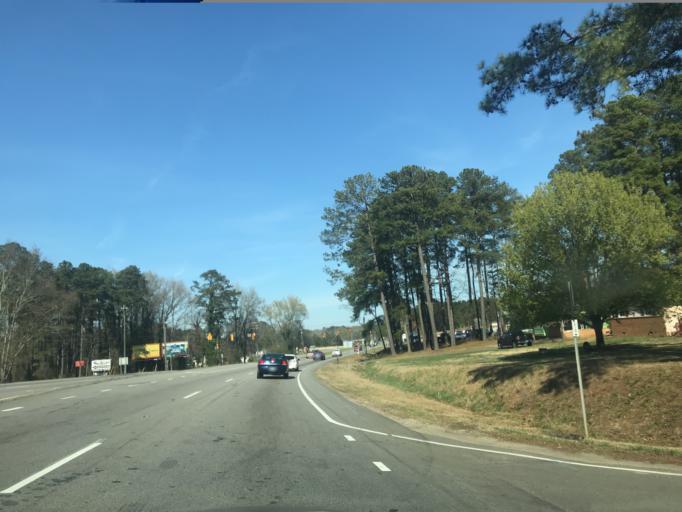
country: US
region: North Carolina
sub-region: Wake County
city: Garner
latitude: 35.7009
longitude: -78.6703
